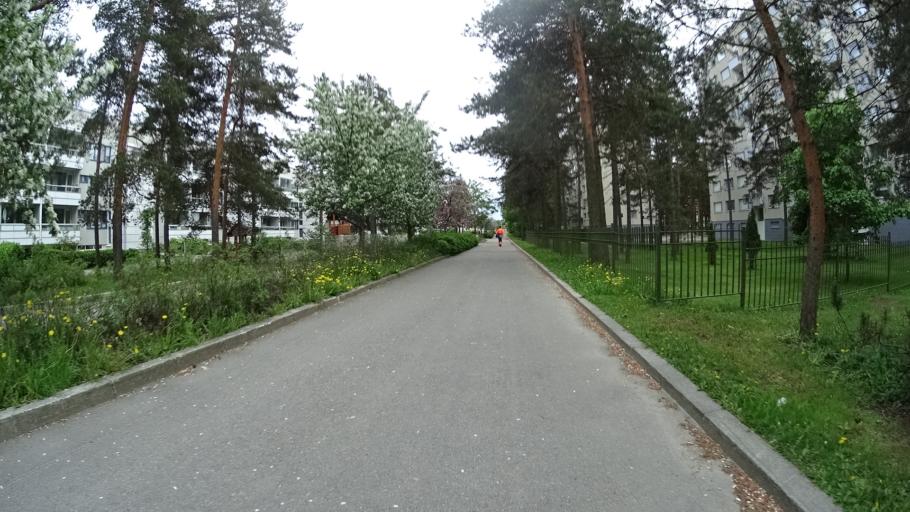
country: FI
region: Uusimaa
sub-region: Helsinki
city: Vantaa
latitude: 60.2392
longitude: 25.0812
